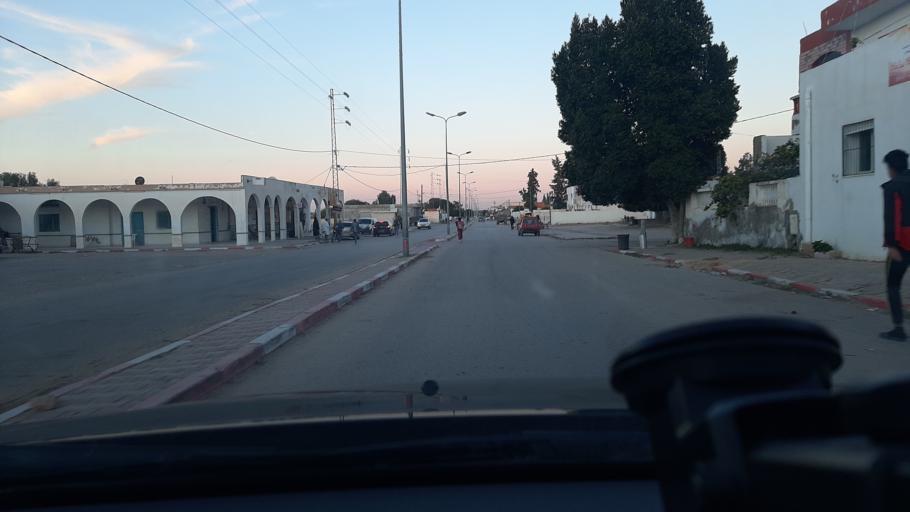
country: TN
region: Al Mahdiyah
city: Shurban
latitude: 34.9623
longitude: 10.3645
